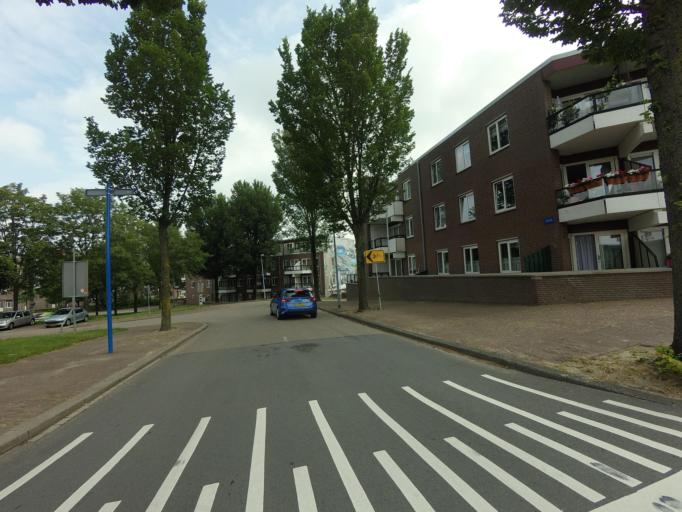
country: NL
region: Flevoland
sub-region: Gemeente Almere
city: Almere Stad
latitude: 52.3341
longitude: 5.2211
